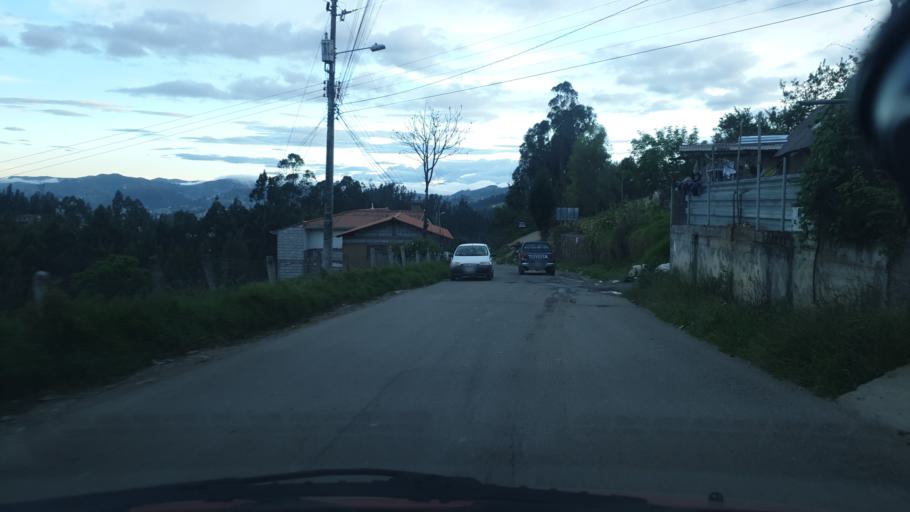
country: EC
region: Azuay
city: Cuenca
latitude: -2.8687
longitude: -79.0719
